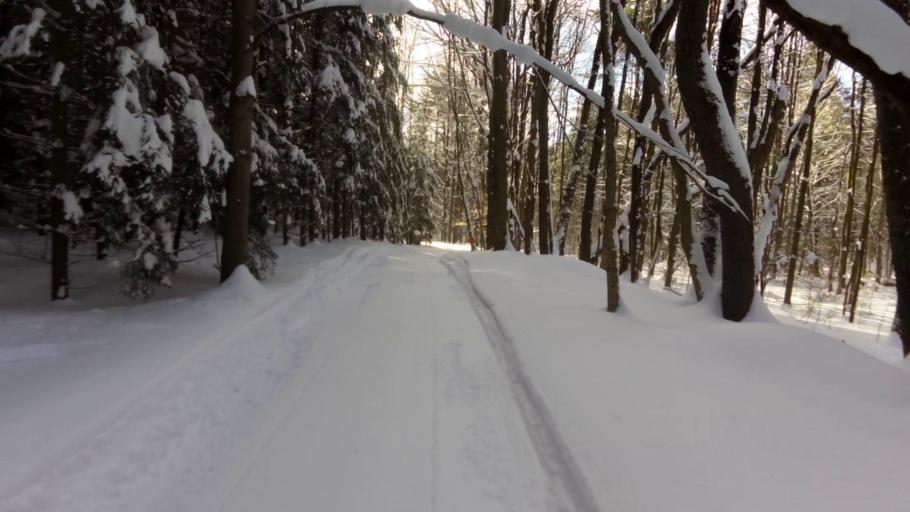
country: US
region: New York
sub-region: Chautauqua County
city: Falconer
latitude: 42.2510
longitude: -79.1505
